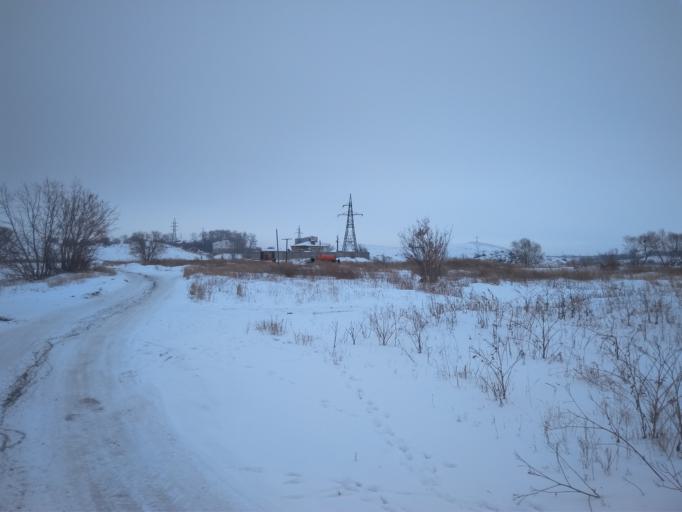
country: RU
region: Chelyabinsk
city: Troitsk
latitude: 54.0830
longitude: 61.5763
